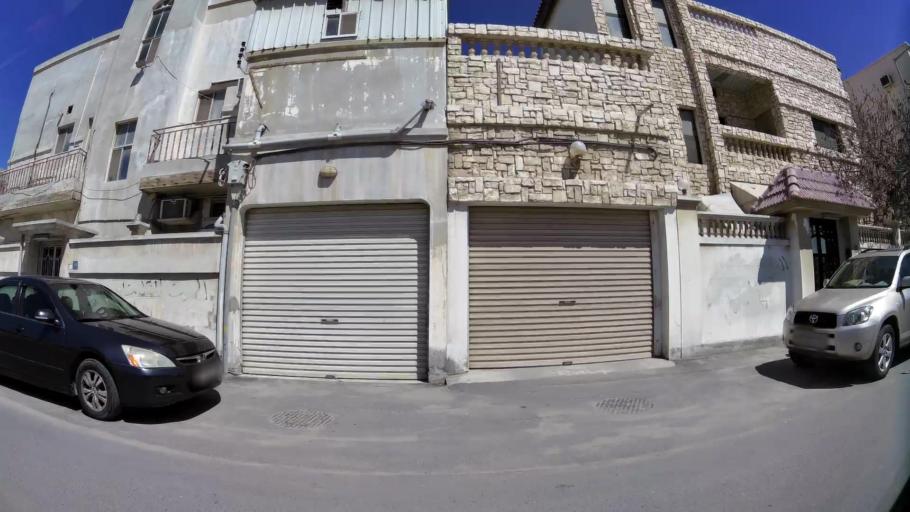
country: BH
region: Muharraq
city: Al Muharraq
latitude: 26.2810
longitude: 50.6331
